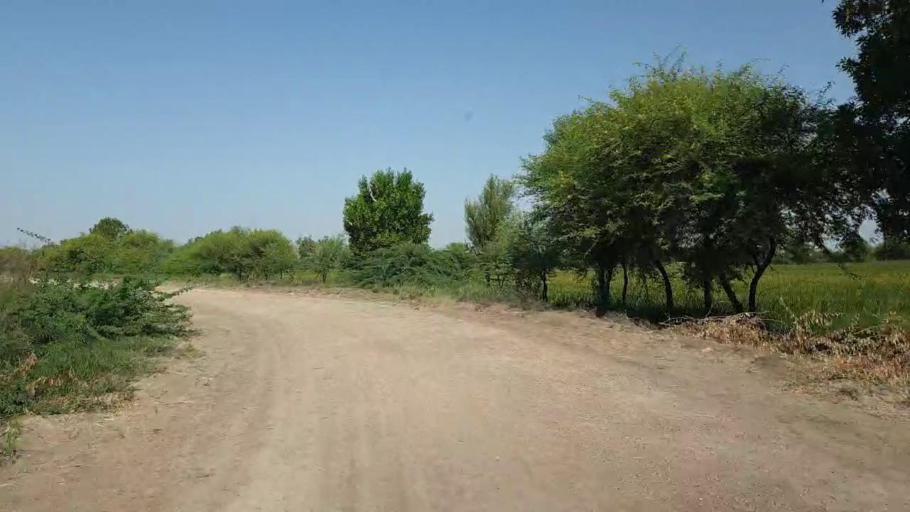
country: PK
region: Sindh
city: Tando Bago
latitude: 24.7394
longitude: 69.0437
